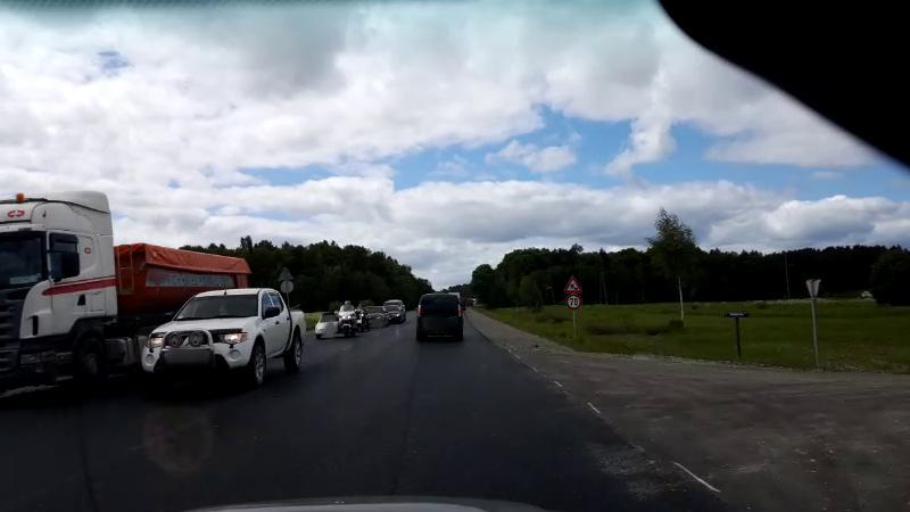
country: LV
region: Salacgrivas
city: Ainazi
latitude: 57.8528
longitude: 24.3599
